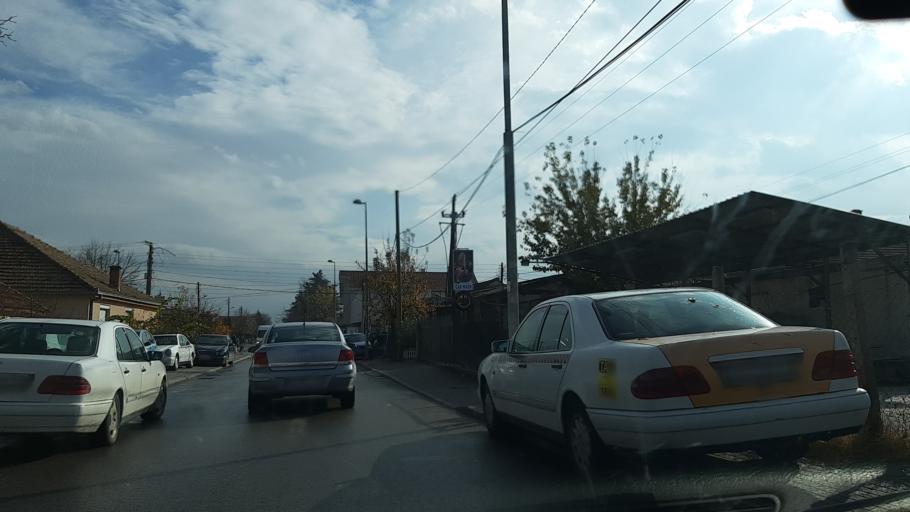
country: MK
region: Kisela Voda
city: Usje
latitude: 41.9776
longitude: 21.4831
